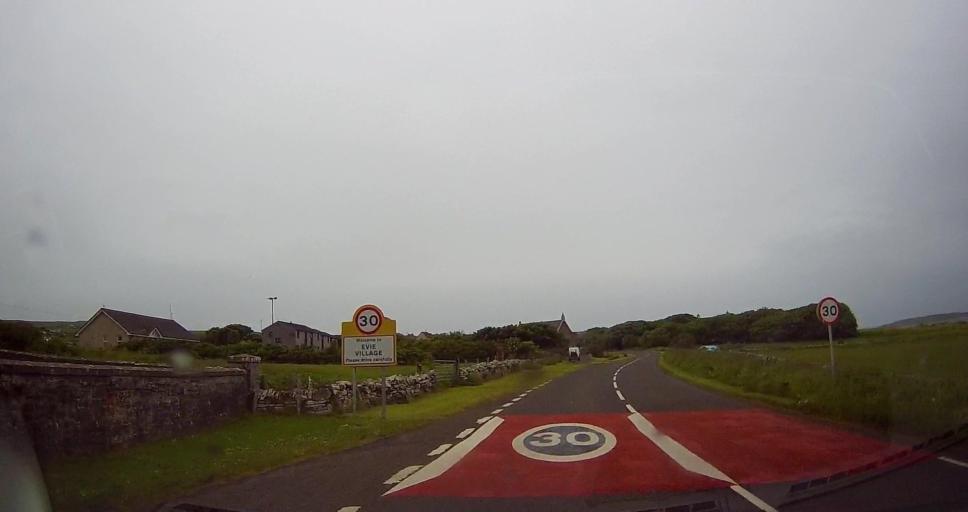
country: GB
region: Scotland
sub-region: Orkney Islands
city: Orkney
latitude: 59.1115
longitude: -3.1027
